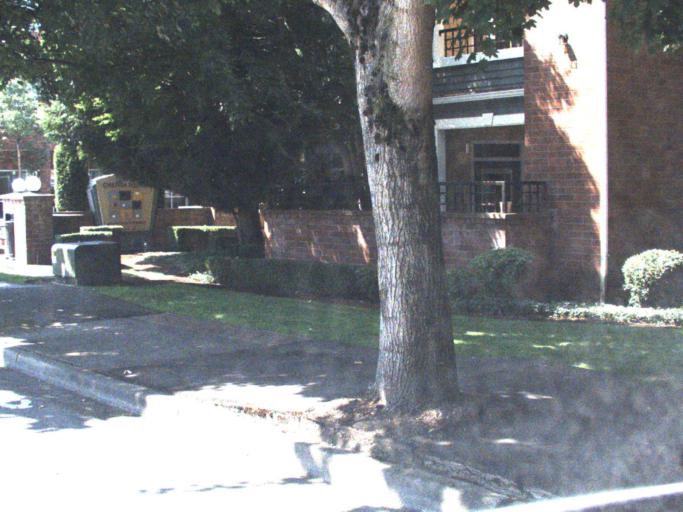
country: US
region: Washington
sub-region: King County
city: Redmond
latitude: 47.6767
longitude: -122.1216
